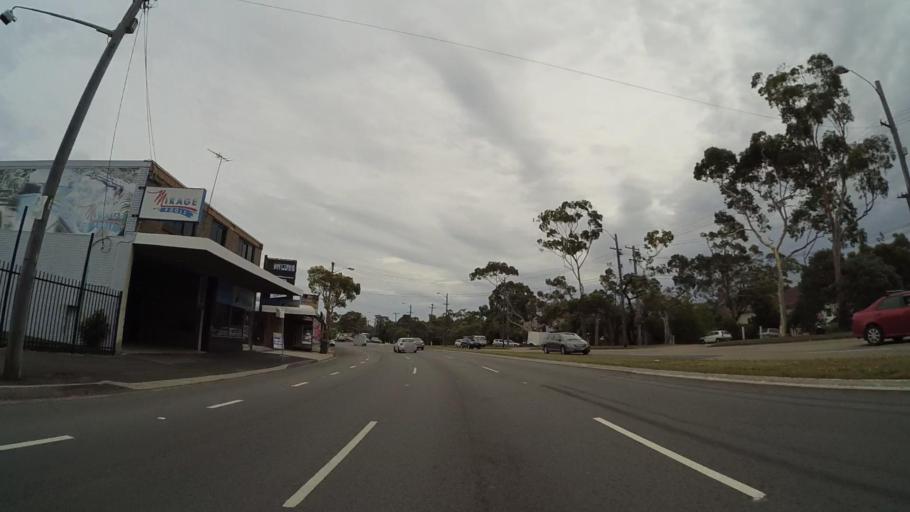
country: AU
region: New South Wales
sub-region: Sutherland Shire
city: Kareela
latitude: -34.0119
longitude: 151.0943
